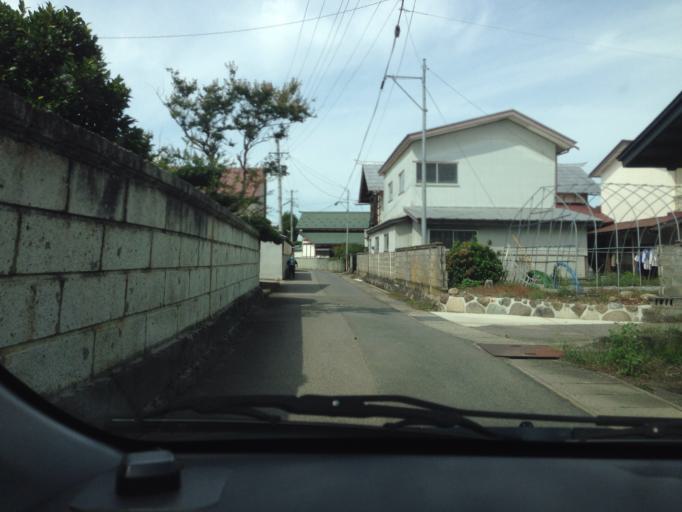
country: JP
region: Fukushima
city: Kitakata
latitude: 37.5400
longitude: 139.8596
